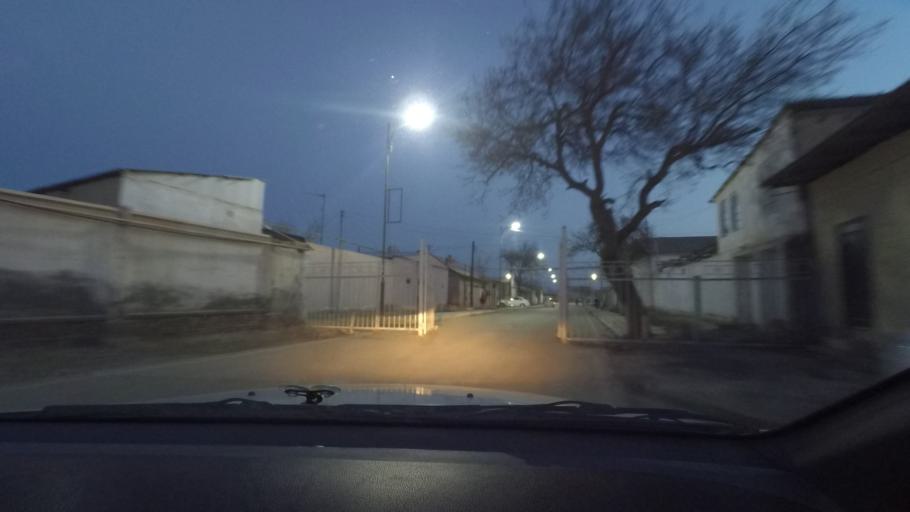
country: UZ
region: Bukhara
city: Bukhara
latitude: 39.7750
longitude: 64.3998
